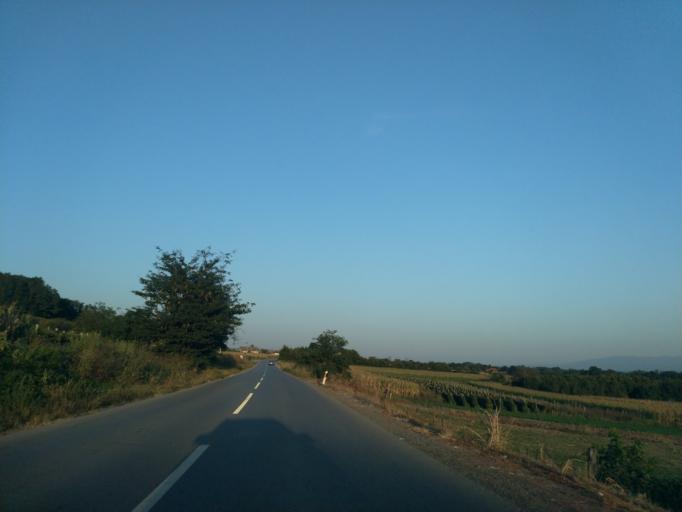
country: RS
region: Central Serbia
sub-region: Rasinski Okrug
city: Trstenik
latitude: 43.6293
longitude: 21.0463
